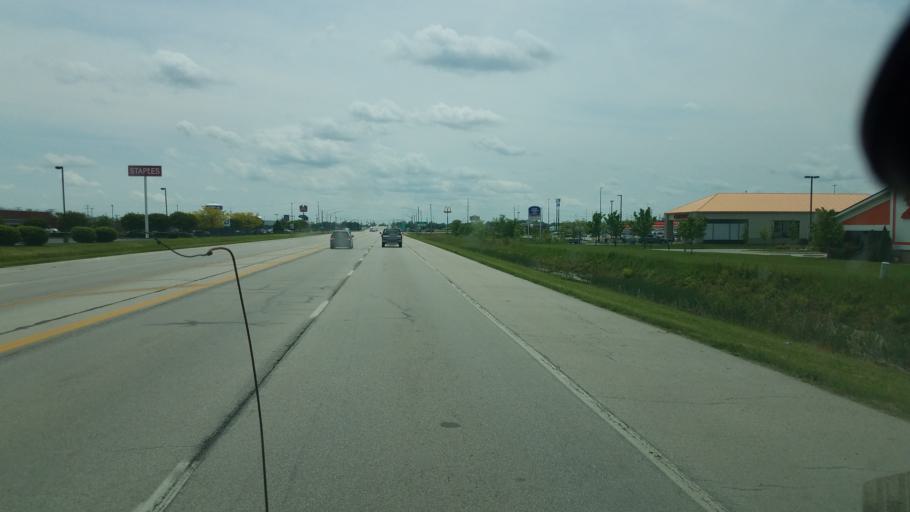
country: US
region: Ohio
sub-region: Sandusky County
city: Fremont
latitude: 41.3766
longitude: -83.1171
